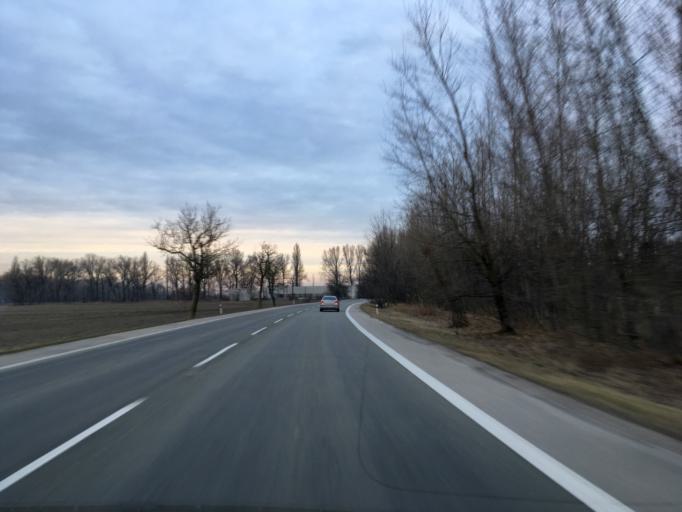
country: SK
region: Trnavsky
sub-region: Okres Dunajska Streda
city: Velky Meder
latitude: 47.9032
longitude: 17.7405
